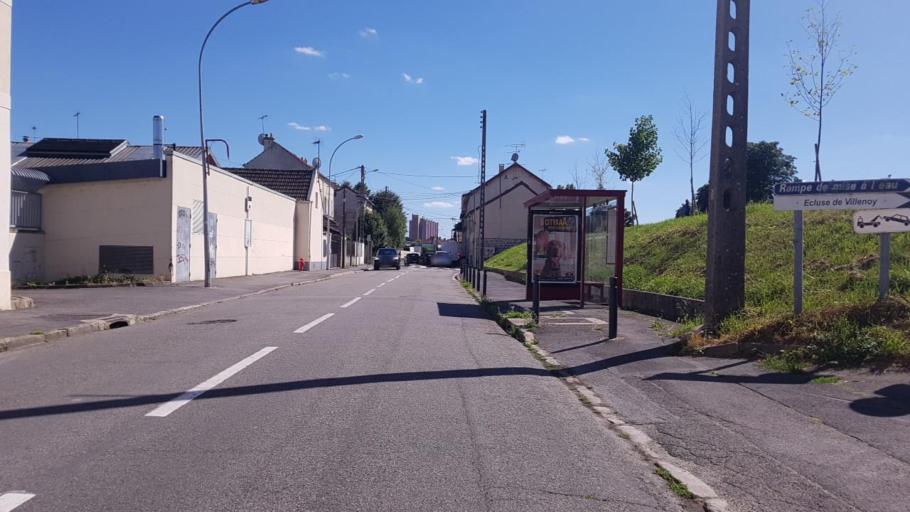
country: FR
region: Ile-de-France
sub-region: Departement de Seine-et-Marne
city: Meaux
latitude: 48.9521
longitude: 2.8710
